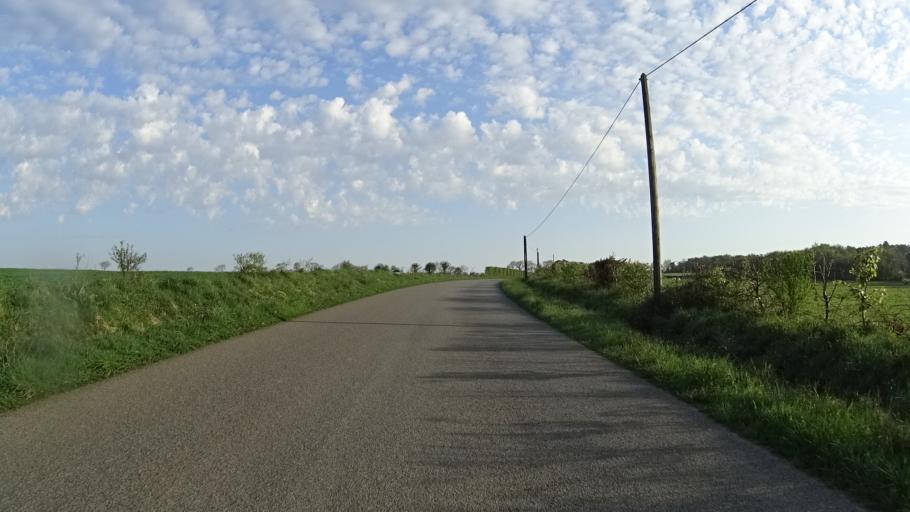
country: FR
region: Brittany
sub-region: Departement du Finistere
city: Sizun
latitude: 48.4214
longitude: -4.0749
